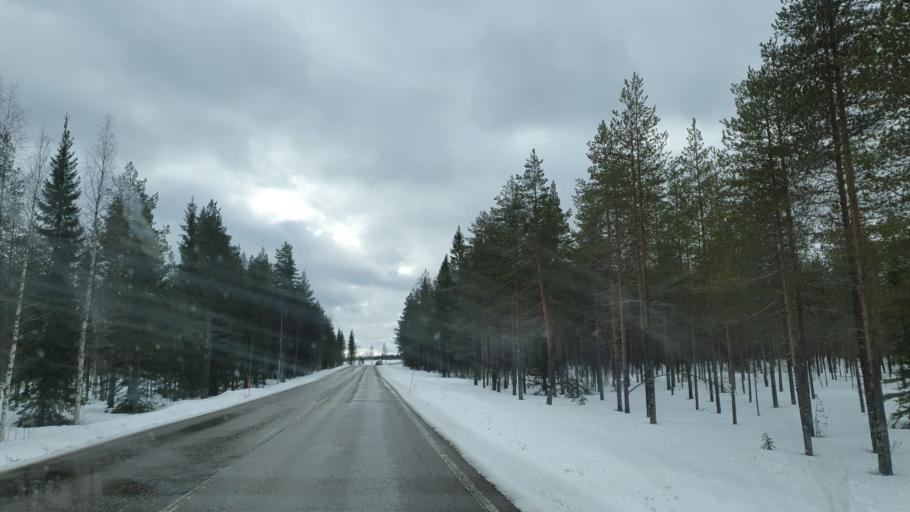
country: FI
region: Kainuu
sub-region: Kehys-Kainuu
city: Puolanka
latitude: 65.0160
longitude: 27.6894
